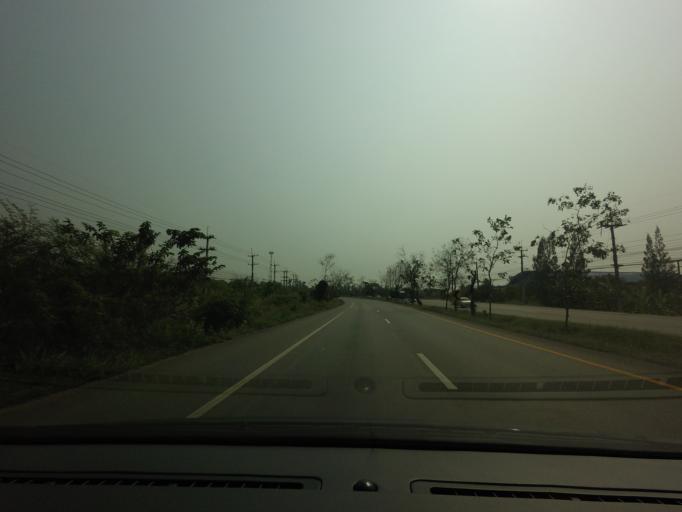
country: TH
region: Prachuap Khiri Khan
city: Sam Roi Yot
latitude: 12.2616
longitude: 99.8693
